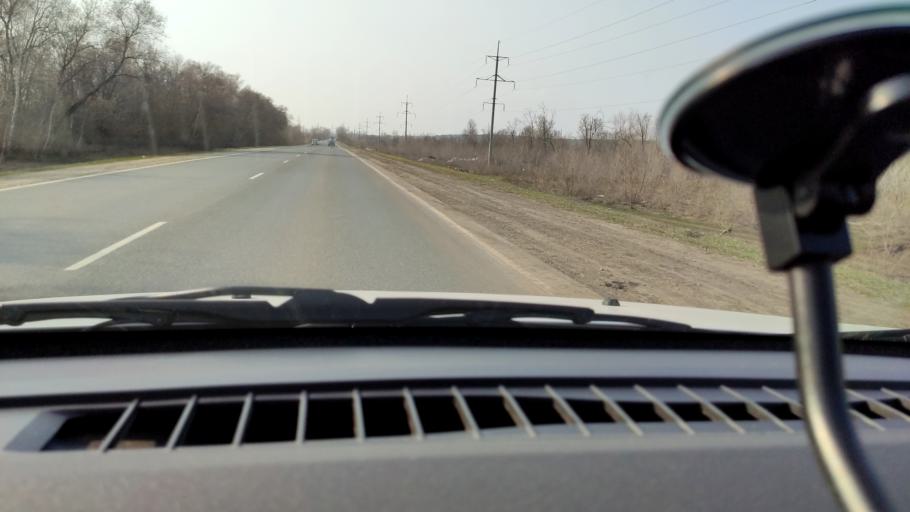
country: RU
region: Samara
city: Dubovyy Umet
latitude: 53.1009
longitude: 50.2577
